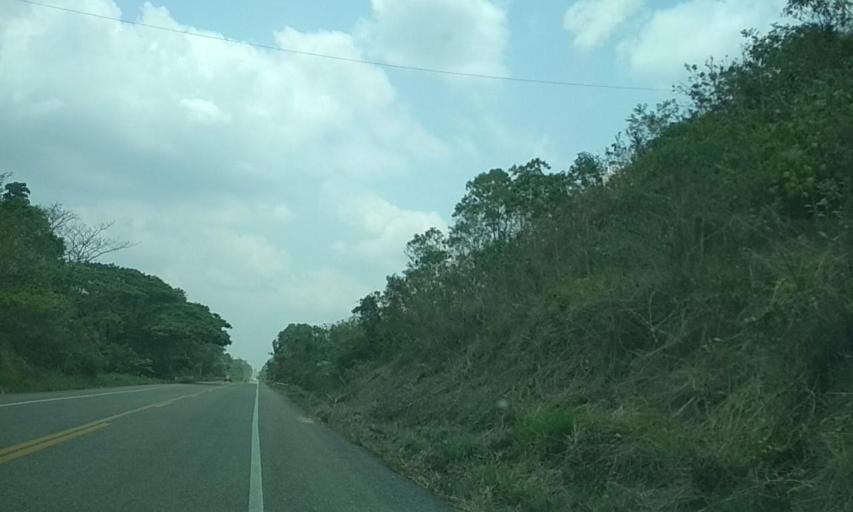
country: MX
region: Tabasco
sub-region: Huimanguillo
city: Francisco Rueda
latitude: 17.6500
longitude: -93.8363
